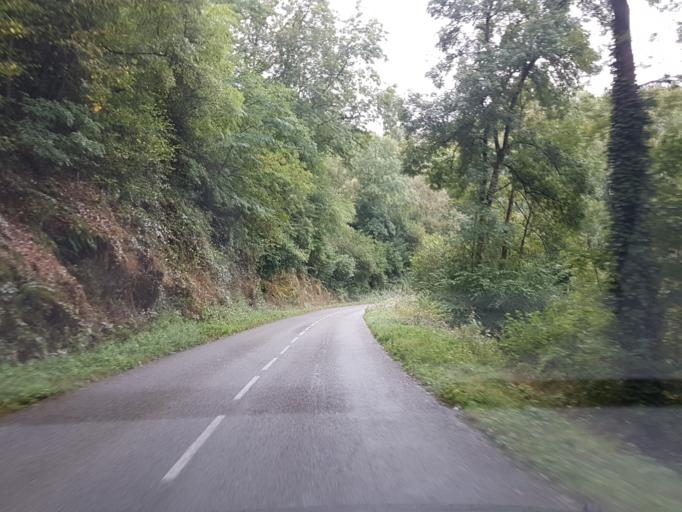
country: FR
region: Midi-Pyrenees
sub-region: Departement de l'Ariege
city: Saint-Girons
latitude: 42.9025
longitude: 1.2419
